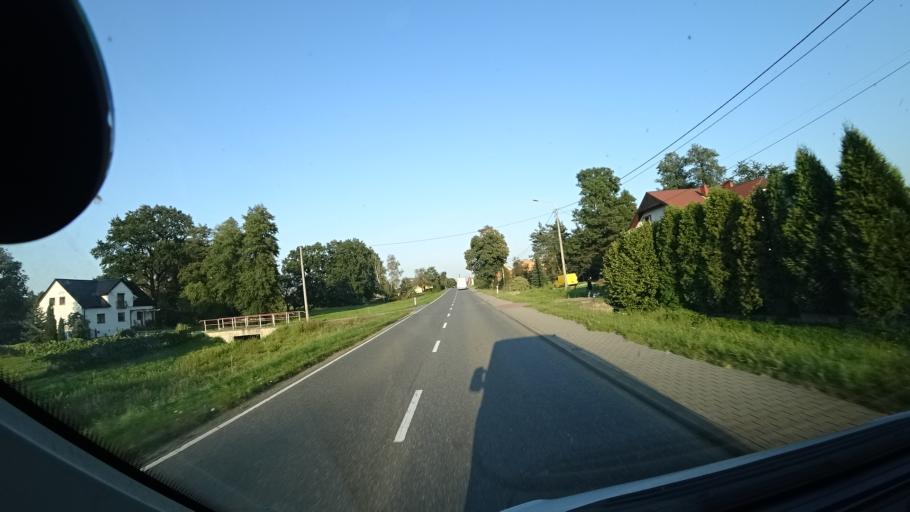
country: PL
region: Silesian Voivodeship
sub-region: Powiat raciborski
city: Rudy
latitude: 50.2694
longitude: 18.4368
